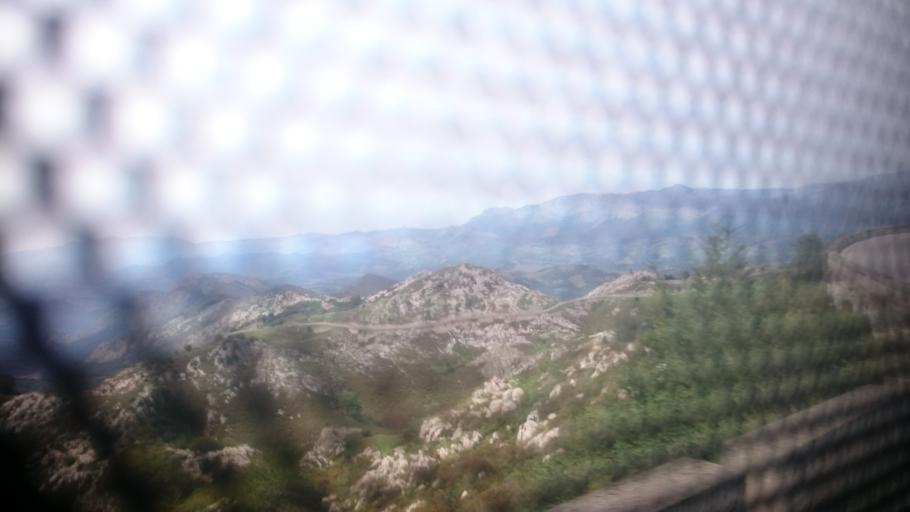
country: ES
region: Asturias
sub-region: Province of Asturias
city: Amieva
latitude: 43.2859
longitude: -5.0080
